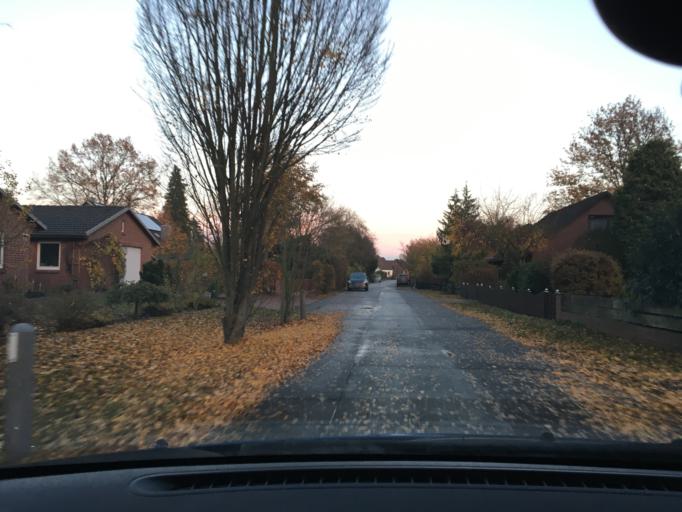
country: DE
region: Lower Saxony
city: Radbruch
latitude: 53.3349
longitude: 10.3081
